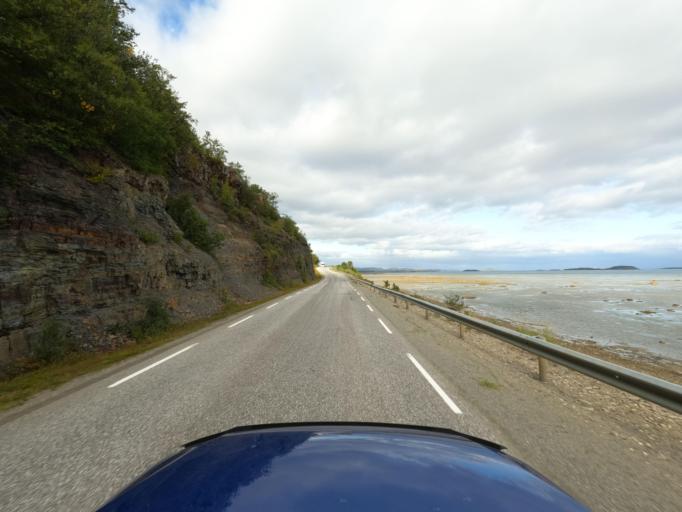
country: NO
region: Finnmark Fylke
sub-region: Porsanger
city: Lakselv
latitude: 70.1289
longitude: 24.9169
